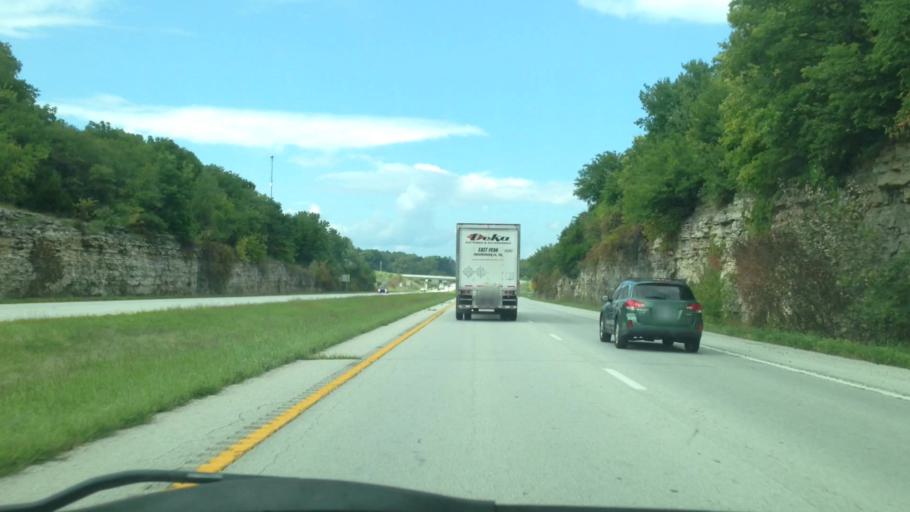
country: US
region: Missouri
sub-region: Marion County
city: Palmyra
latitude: 39.8046
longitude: -91.5162
